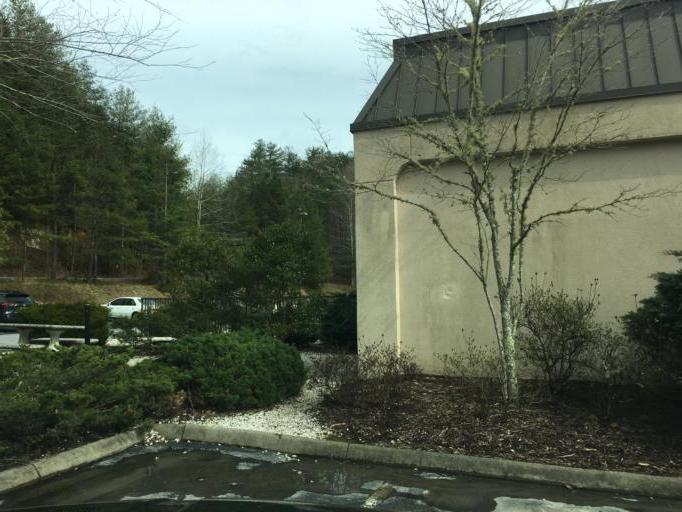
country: US
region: North Carolina
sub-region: Transylvania County
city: Brevard
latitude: 35.2782
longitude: -82.7023
